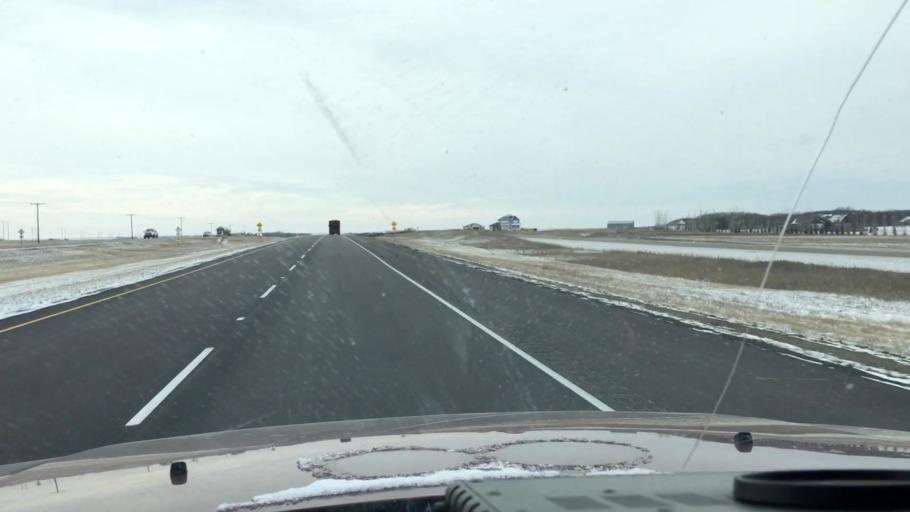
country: CA
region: Saskatchewan
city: Saskatoon
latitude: 51.9318
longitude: -106.5362
